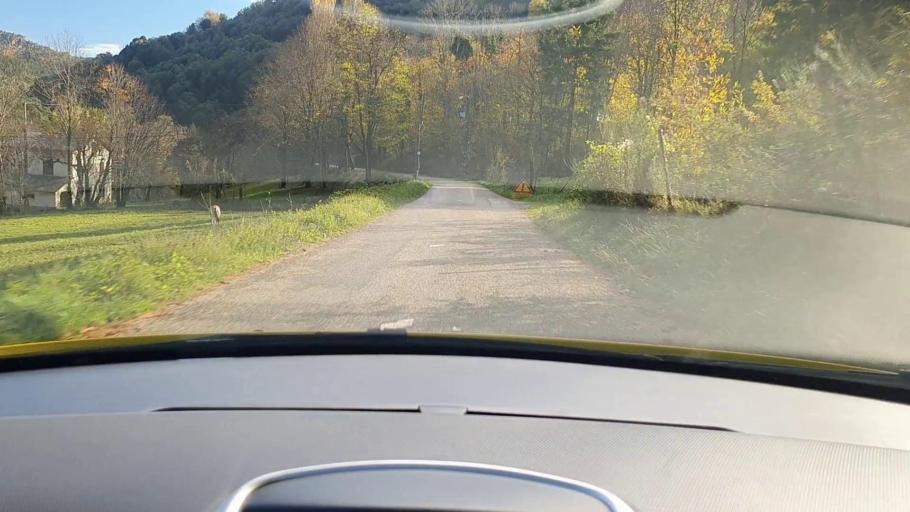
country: FR
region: Languedoc-Roussillon
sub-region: Departement du Gard
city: Valleraugue
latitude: 44.1637
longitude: 3.6626
